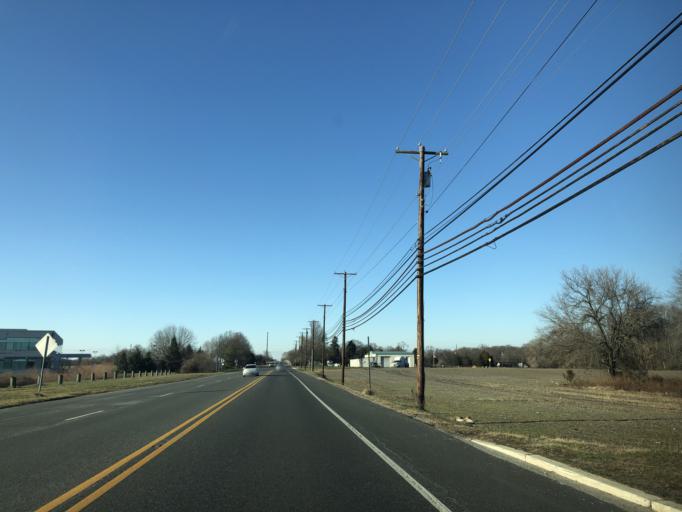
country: US
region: New Jersey
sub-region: Salem County
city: Carneys Point
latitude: 39.7038
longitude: -75.4415
